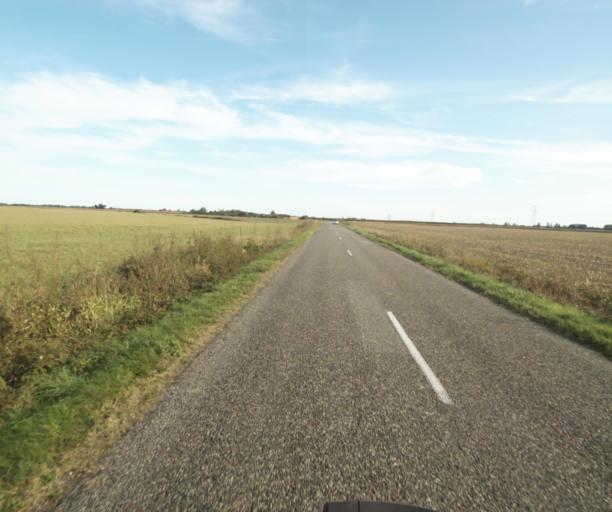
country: FR
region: Midi-Pyrenees
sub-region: Departement du Tarn-et-Garonne
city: Finhan
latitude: 43.9083
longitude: 1.1159
